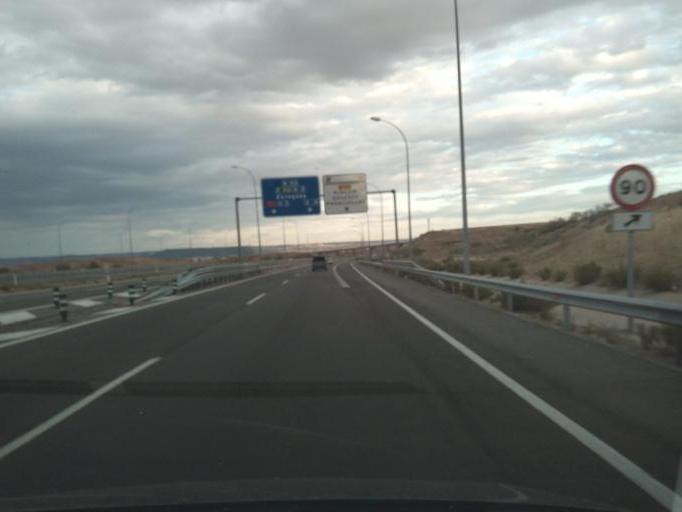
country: ES
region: Madrid
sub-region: Provincia de Madrid
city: Paracuellos de Jarama
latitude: 40.5217
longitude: -3.5071
